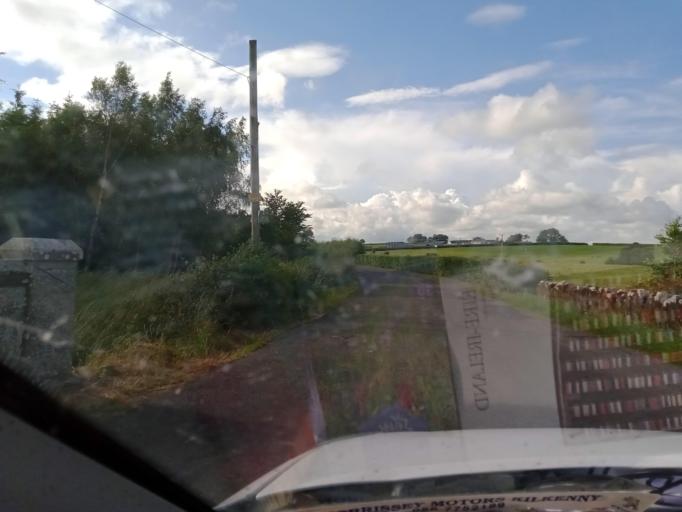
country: IE
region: Leinster
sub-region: Laois
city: Rathdowney
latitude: 52.7832
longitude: -7.5469
